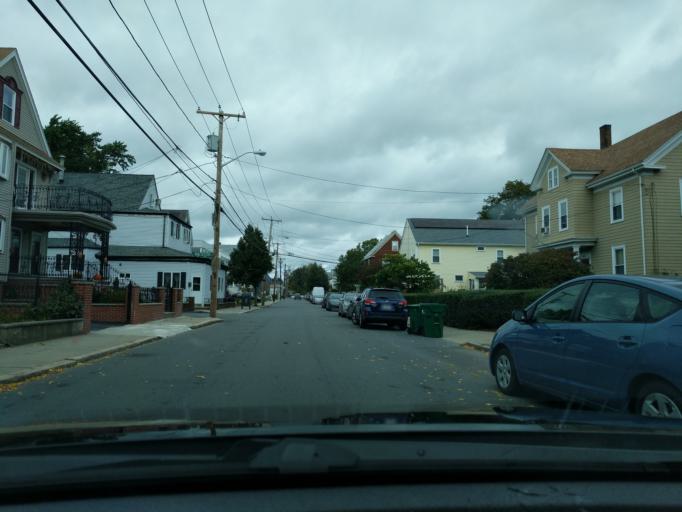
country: US
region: Massachusetts
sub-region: Middlesex County
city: Medford
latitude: 42.4013
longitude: -71.1111
